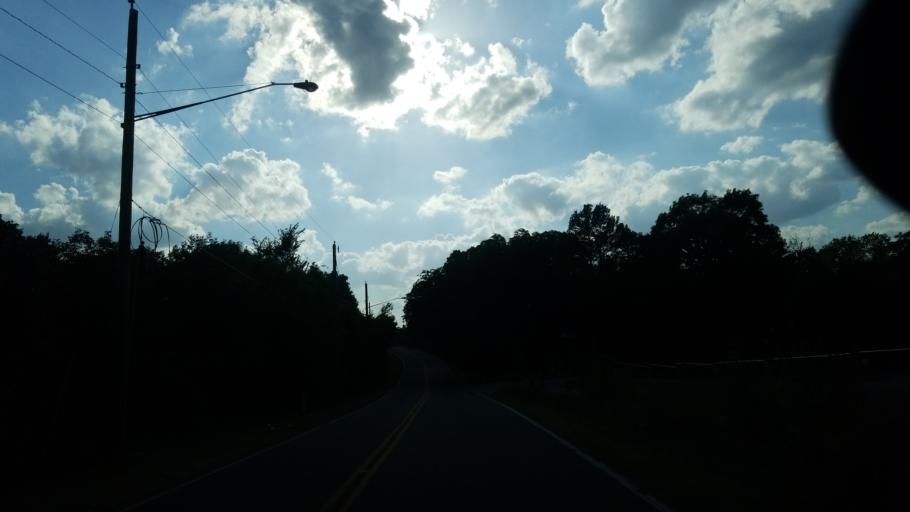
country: US
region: Texas
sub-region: Dallas County
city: Dallas
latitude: 32.7793
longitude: -96.7088
